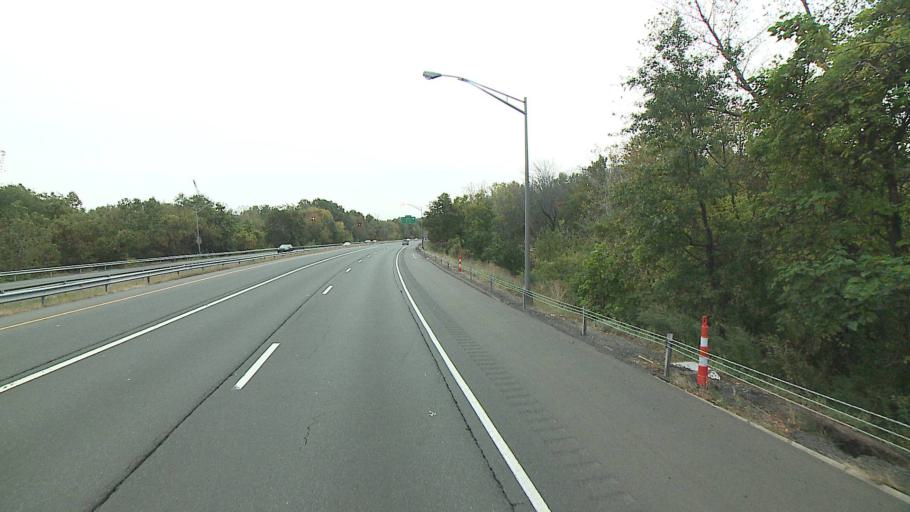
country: US
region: Connecticut
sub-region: Hartford County
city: Kensington
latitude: 41.6441
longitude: -72.7582
